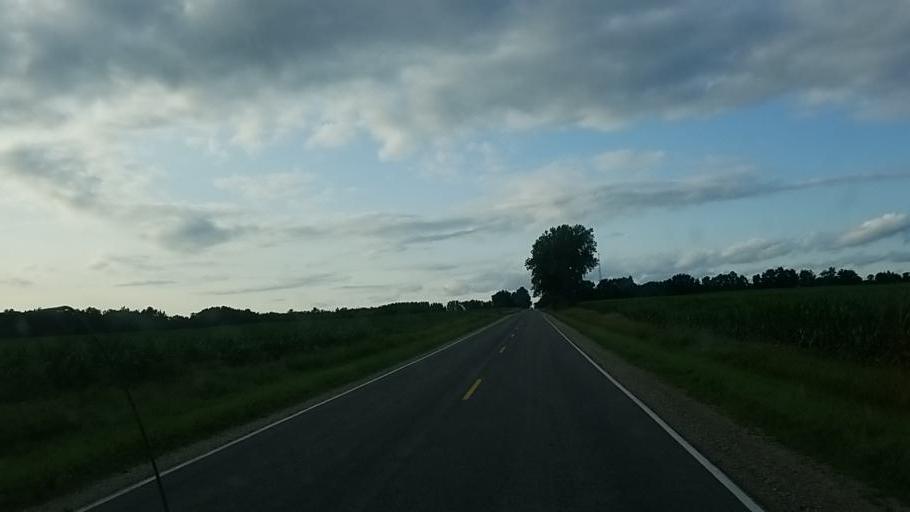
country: US
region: Michigan
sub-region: Montcalm County
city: Lakeview
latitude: 43.3432
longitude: -85.3235
